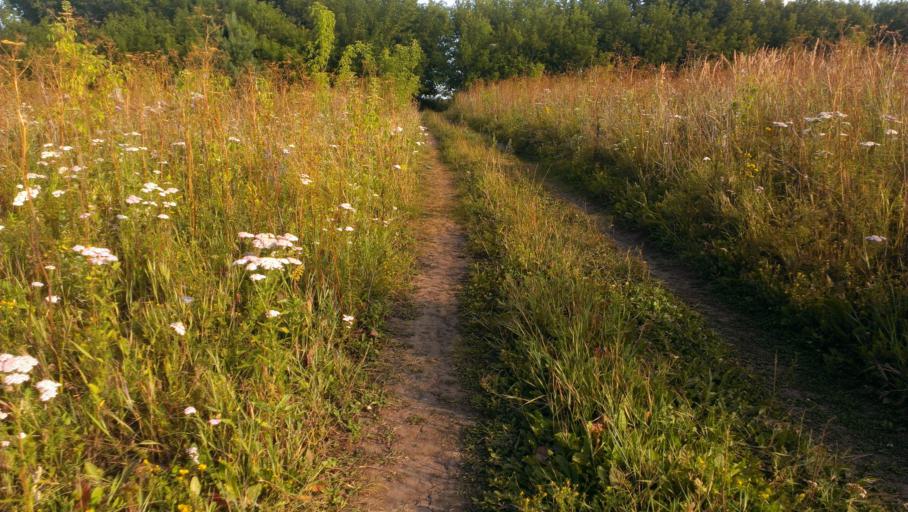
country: RU
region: Altai Krai
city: Gon'ba
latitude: 53.3878
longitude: 83.5994
